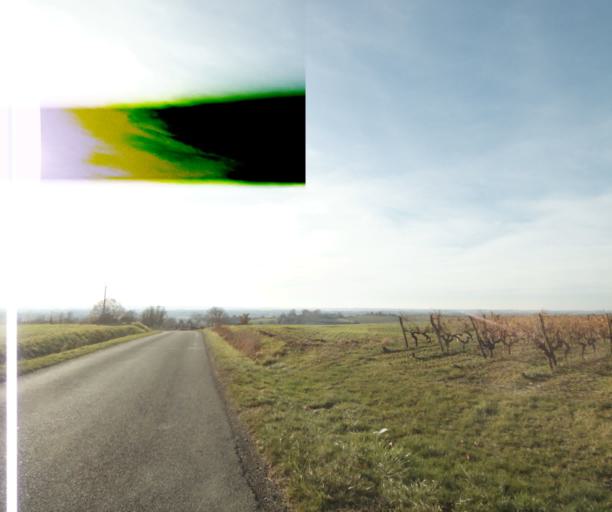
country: FR
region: Poitou-Charentes
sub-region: Departement de la Charente-Maritime
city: Chaniers
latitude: 45.7275
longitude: -0.5508
